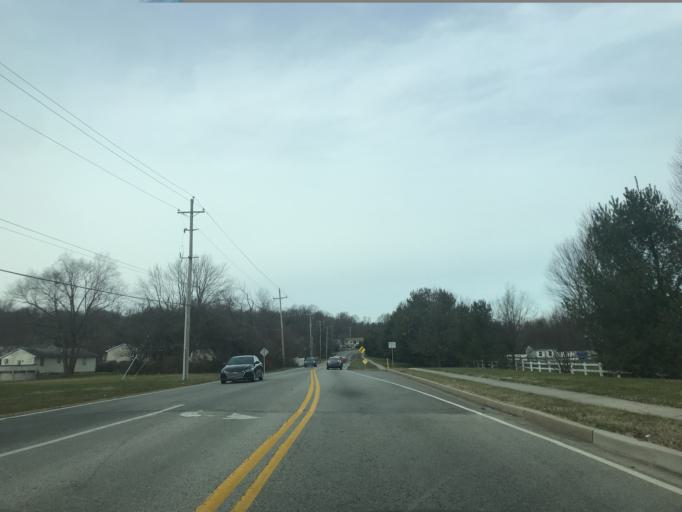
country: US
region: Maryland
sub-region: Cecil County
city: Elkton
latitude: 39.6082
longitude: -75.7906
